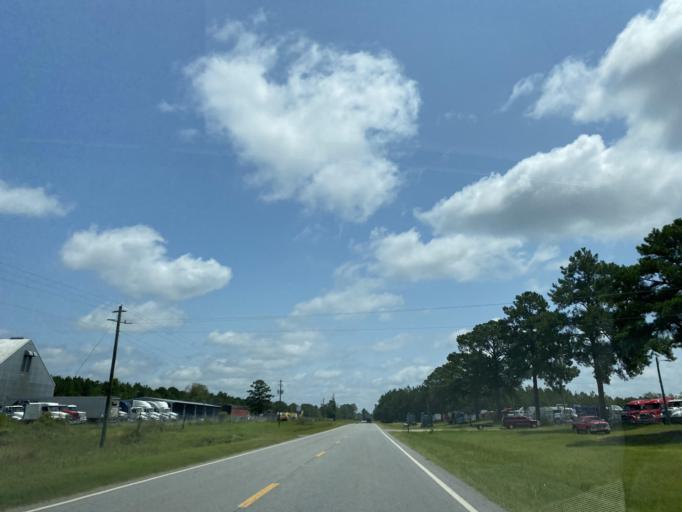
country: US
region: Georgia
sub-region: Telfair County
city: Helena
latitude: 32.0241
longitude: -83.0414
